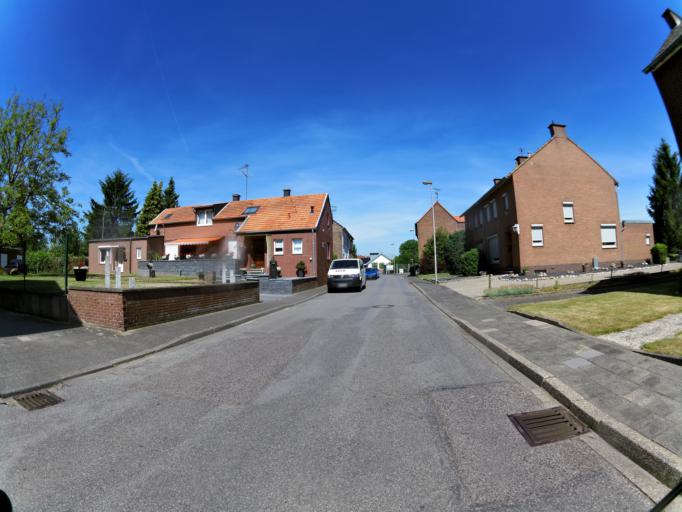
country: NL
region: Limburg
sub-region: Gemeente Sittard-Geleen
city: Sittard
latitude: 51.0137
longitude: 5.8938
